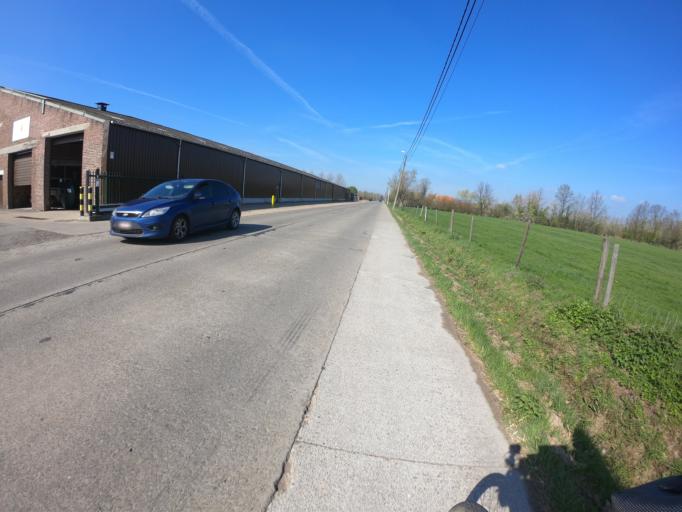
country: BE
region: Flanders
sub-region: Provincie Vlaams-Brabant
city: Geetbets
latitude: 50.8972
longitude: 5.1465
